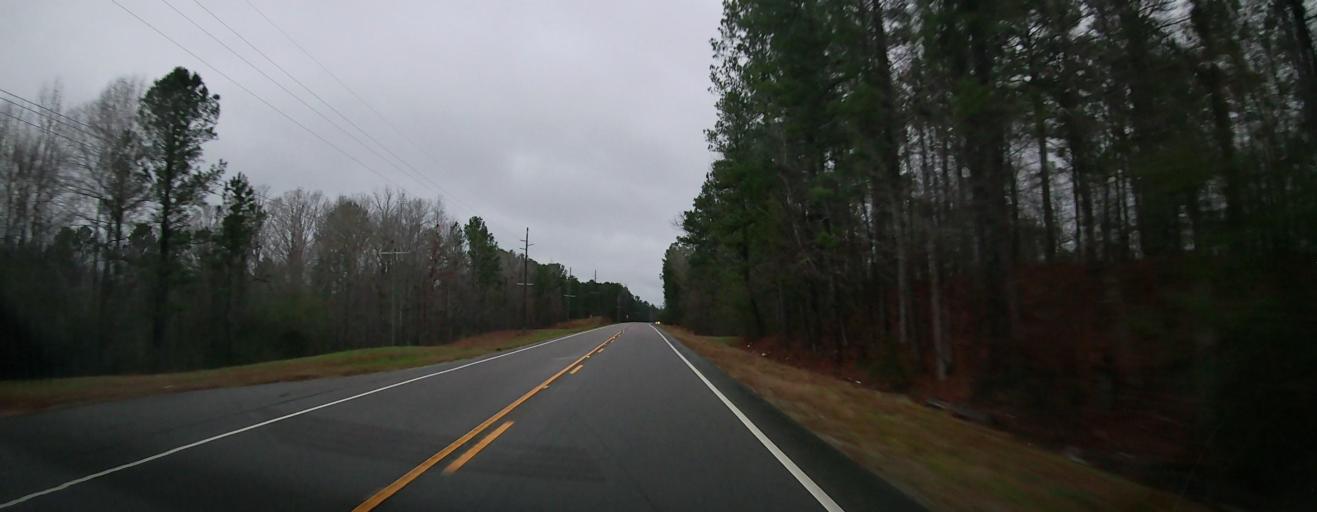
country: US
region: Alabama
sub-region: Bibb County
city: West Blocton
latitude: 33.0894
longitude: -87.1375
